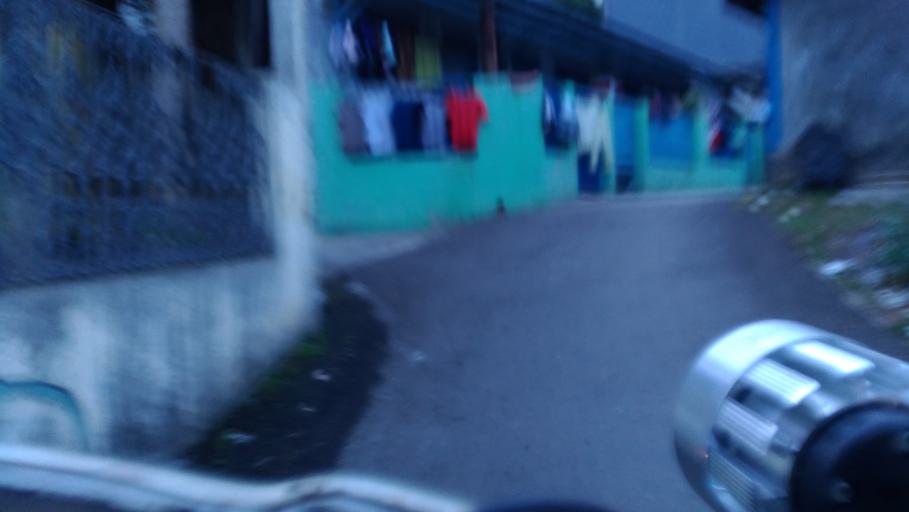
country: ID
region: West Java
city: Depok
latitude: -6.3530
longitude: 106.8756
